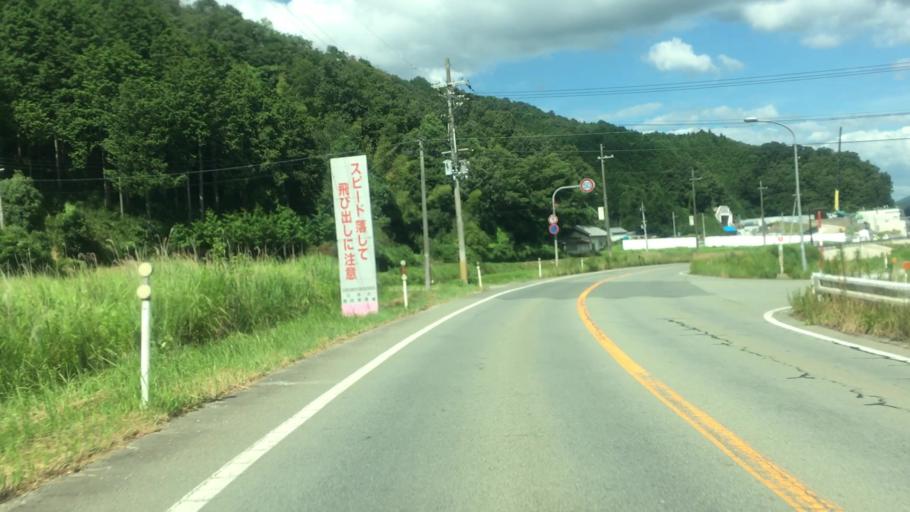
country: JP
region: Hyogo
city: Toyooka
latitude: 35.4684
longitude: 134.7584
